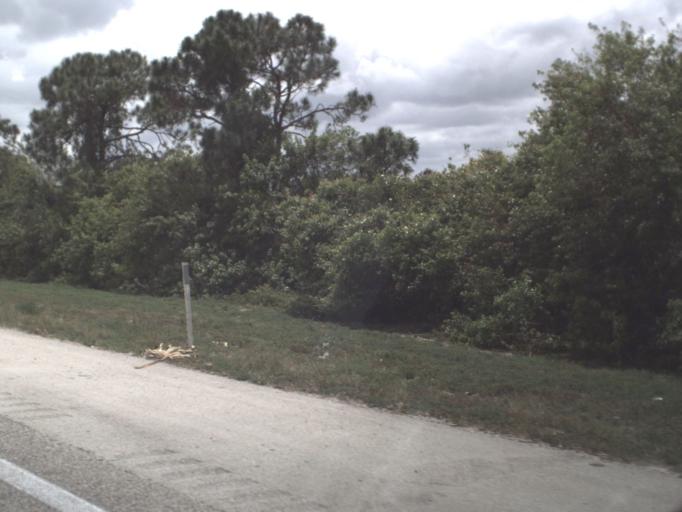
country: US
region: Florida
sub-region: Brevard County
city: South Patrick Shores
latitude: 28.2189
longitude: -80.7154
